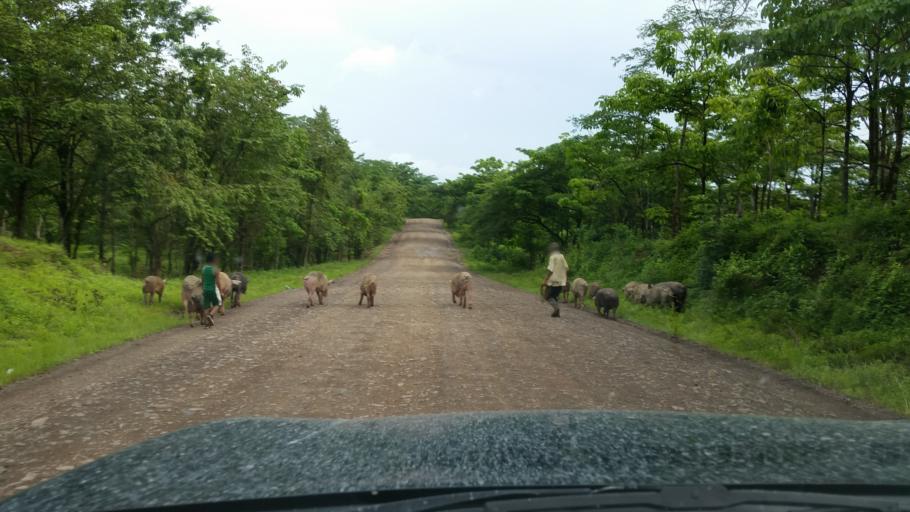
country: NI
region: Atlantico Norte (RAAN)
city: Siuna
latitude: 13.4650
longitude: -84.8482
